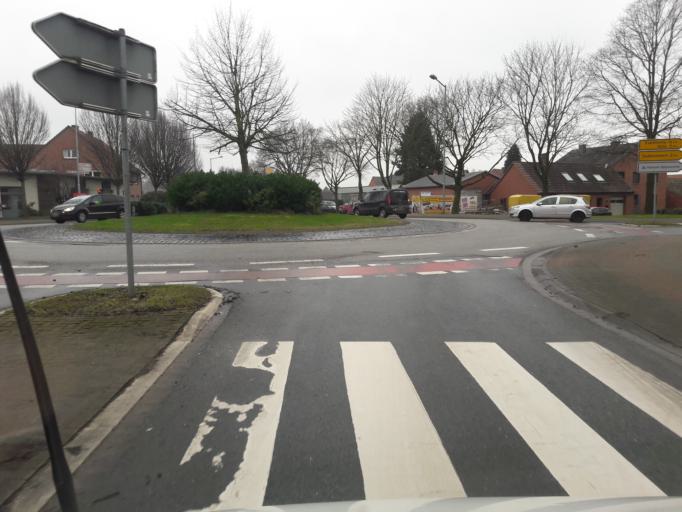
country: DE
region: North Rhine-Westphalia
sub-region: Regierungsbezirk Detmold
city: Hille
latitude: 52.3138
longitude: 8.8206
